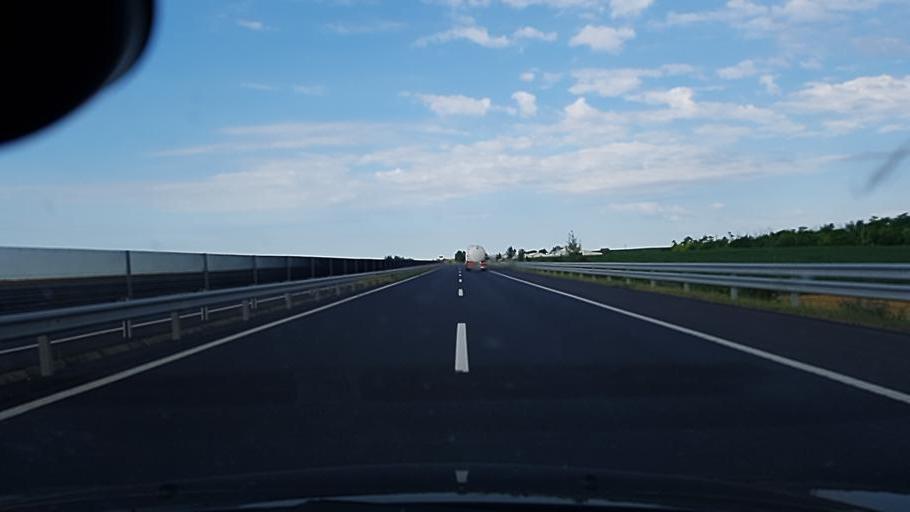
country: HU
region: Fejer
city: Rackeresztur
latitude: 47.2526
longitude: 18.8395
